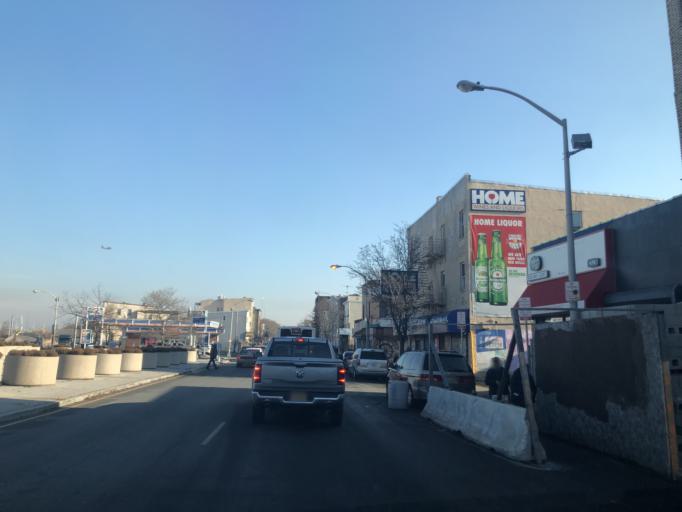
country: US
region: New Jersey
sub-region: Essex County
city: Newark
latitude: 40.7326
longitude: -74.1586
